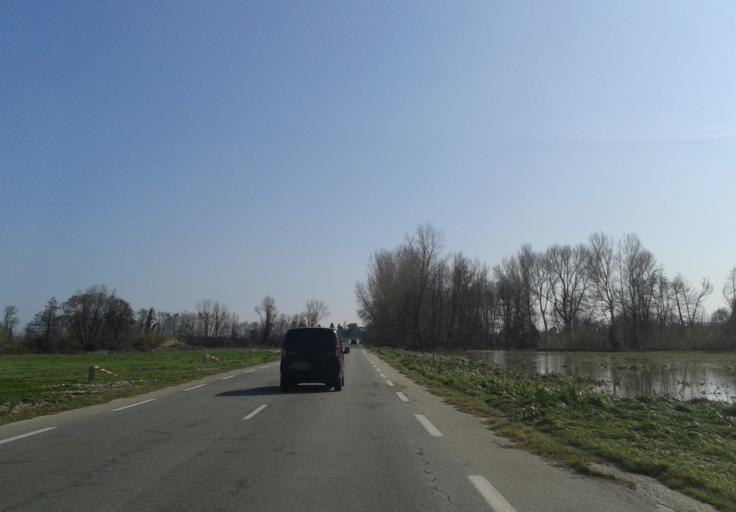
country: FR
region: Corsica
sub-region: Departement de la Haute-Corse
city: Cervione
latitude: 42.2912
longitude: 9.5480
